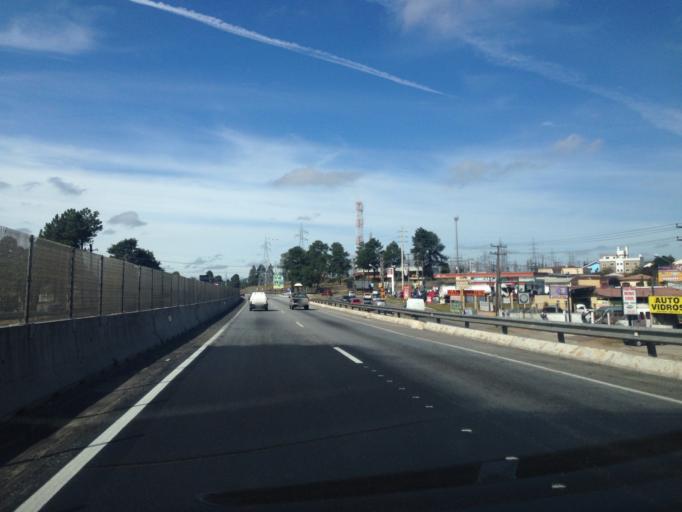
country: BR
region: Parana
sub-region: Pinhais
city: Pinhais
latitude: -25.4730
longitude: -49.2101
